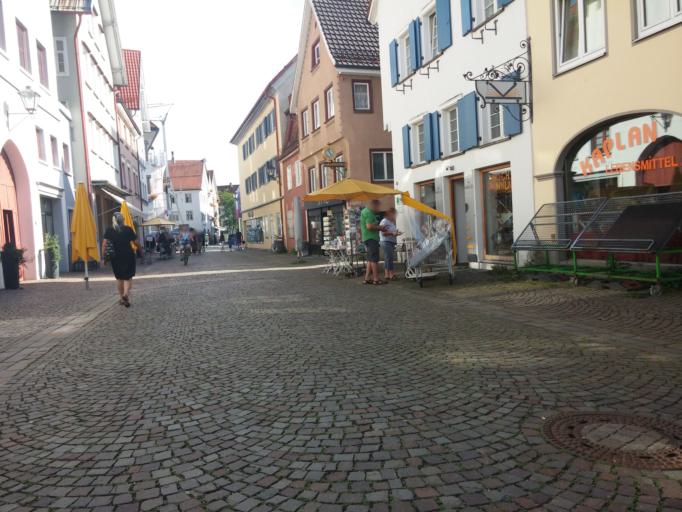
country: DE
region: Baden-Wuerttemberg
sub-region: Tuebingen Region
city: Leutkirch im Allgau
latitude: 47.8274
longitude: 10.0239
